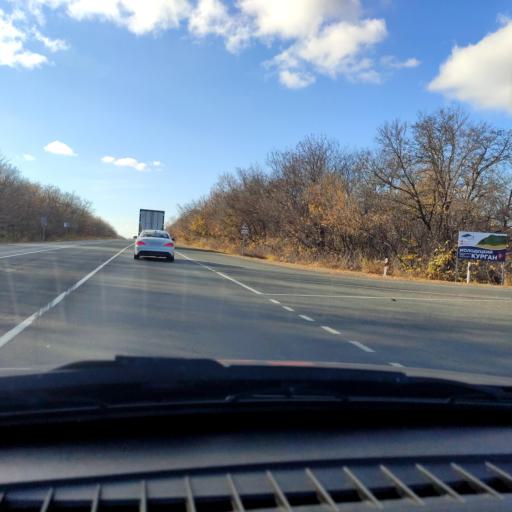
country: RU
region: Samara
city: Zhigulevsk
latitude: 53.3225
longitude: 49.3902
